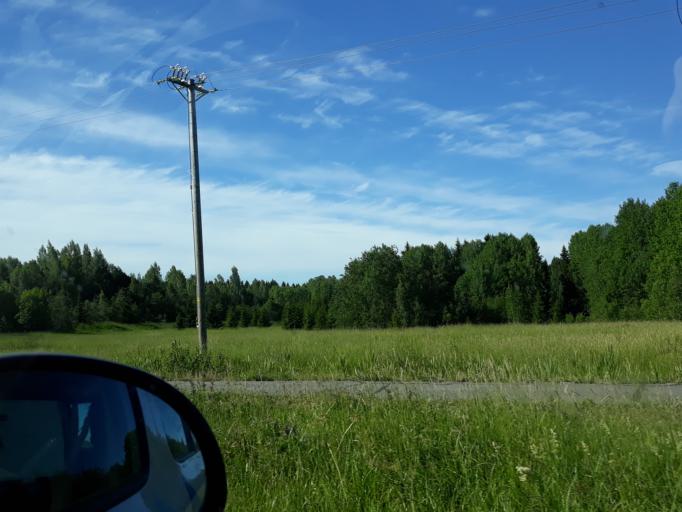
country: FI
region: Uusimaa
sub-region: Helsinki
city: Jaervenpaeae
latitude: 60.5481
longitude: 24.9799
